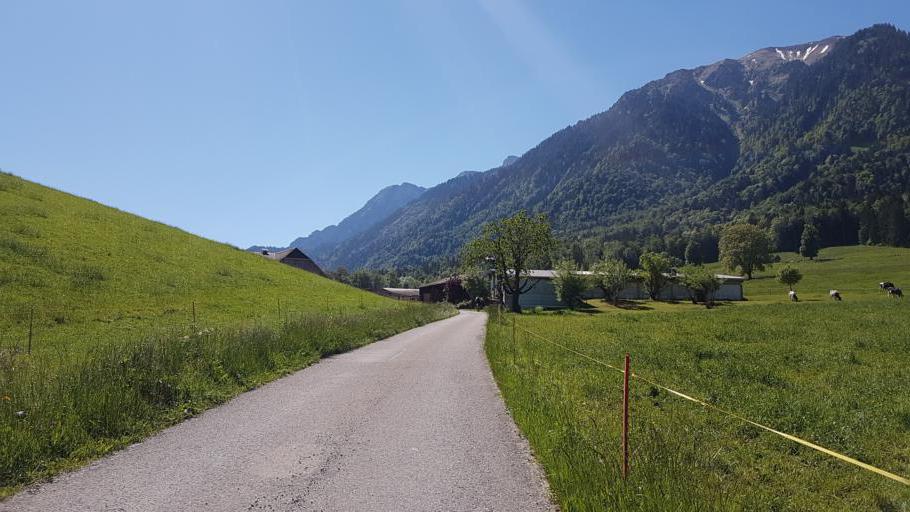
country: CH
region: Bern
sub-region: Thun District
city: Blumenstein
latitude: 46.7283
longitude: 7.5229
